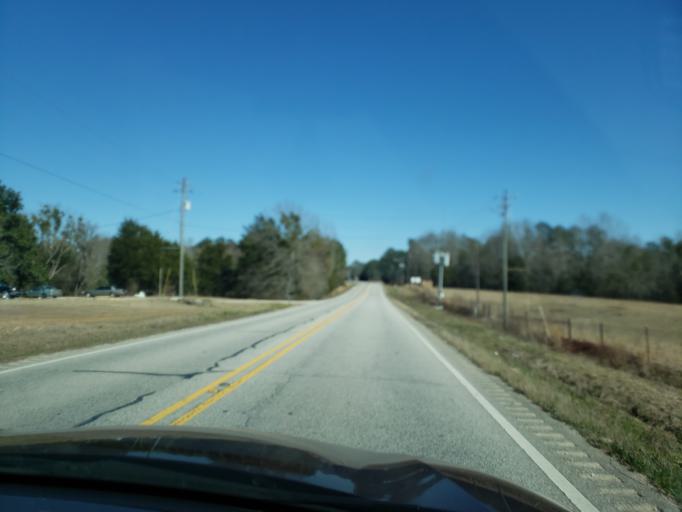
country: US
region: Alabama
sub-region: Lee County
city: Auburn
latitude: 32.5885
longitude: -85.6460
